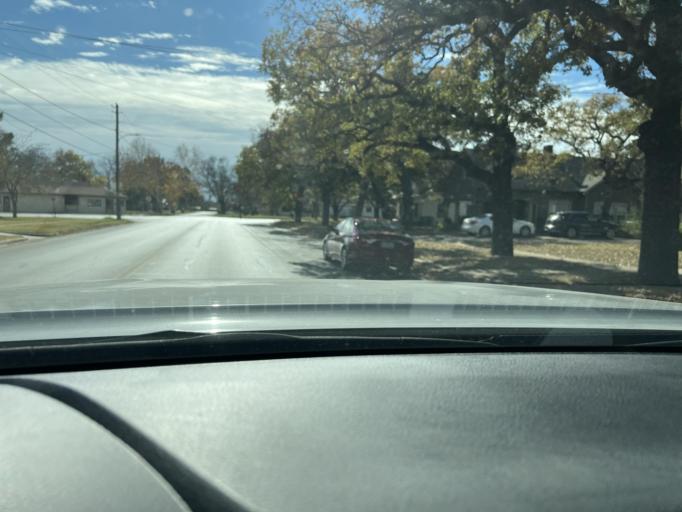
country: US
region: Texas
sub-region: Eastland County
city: Eastland
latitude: 32.3898
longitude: -98.8182
